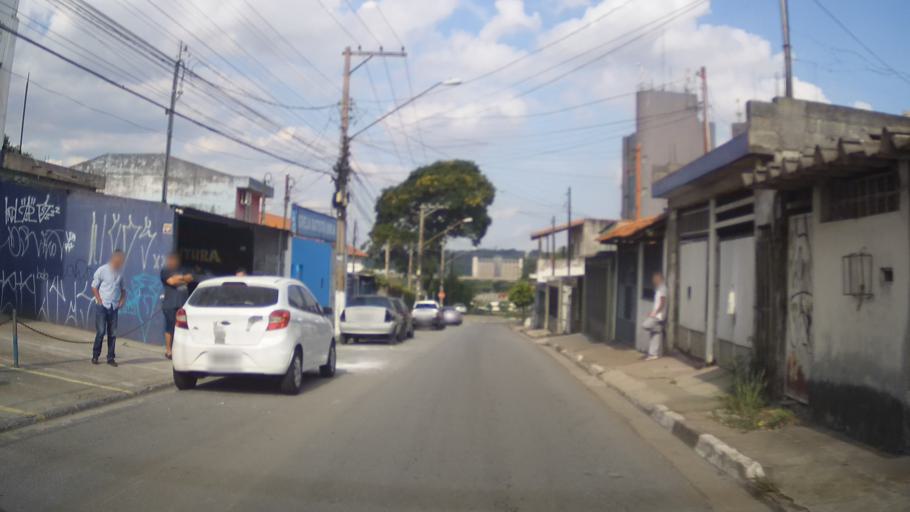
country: BR
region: Sao Paulo
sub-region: Guarulhos
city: Guarulhos
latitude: -23.4528
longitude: -46.5039
